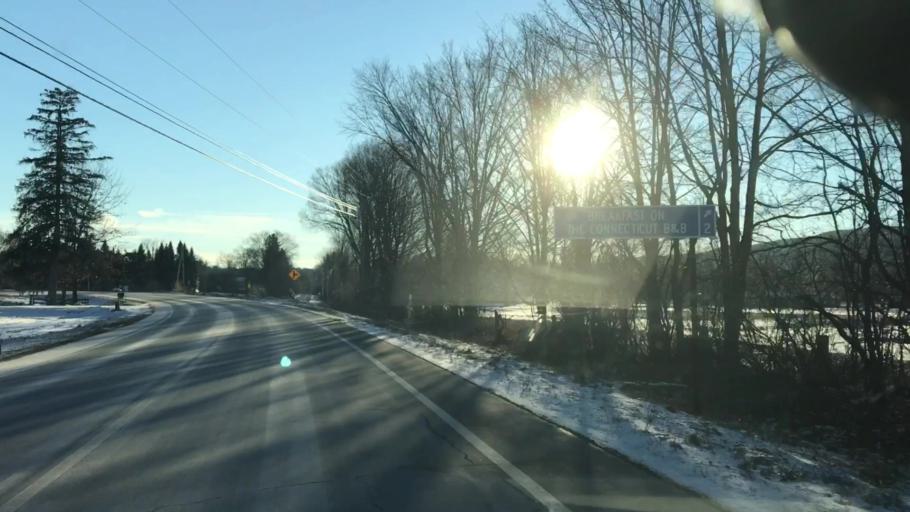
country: US
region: New Hampshire
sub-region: Grafton County
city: Orford
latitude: 43.8811
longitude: -72.1553
